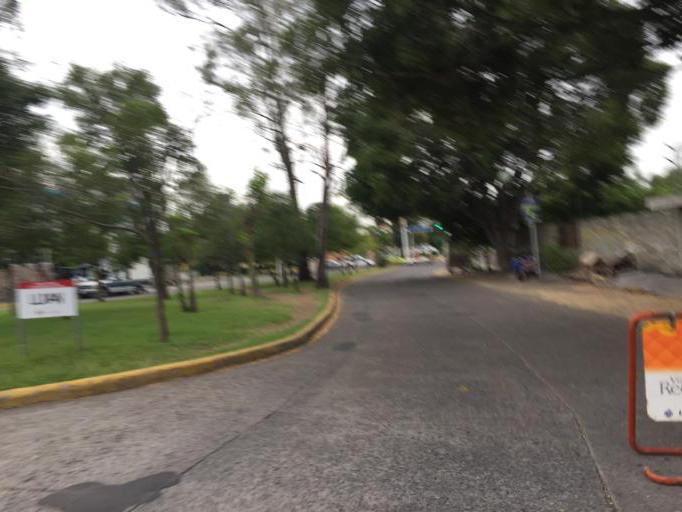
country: MX
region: Jalisco
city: Guadalajara
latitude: 20.6657
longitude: -103.3855
